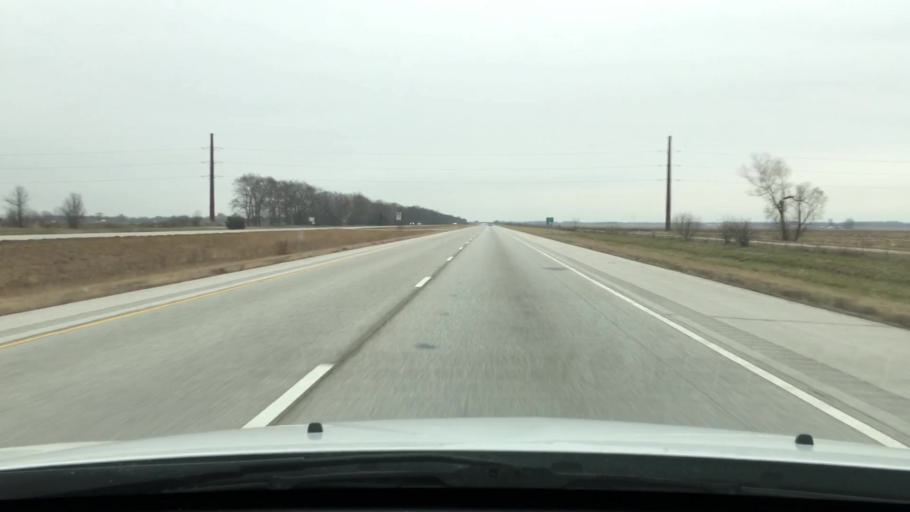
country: US
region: Illinois
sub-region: Scott County
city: Winchester
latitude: 39.6801
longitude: -90.3753
